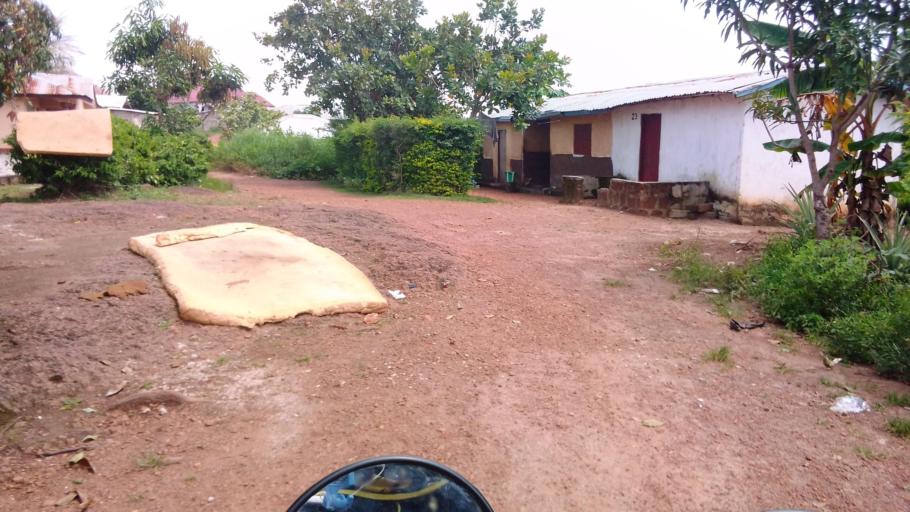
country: SL
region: Northern Province
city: Makeni
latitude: 8.8814
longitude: -12.0282
